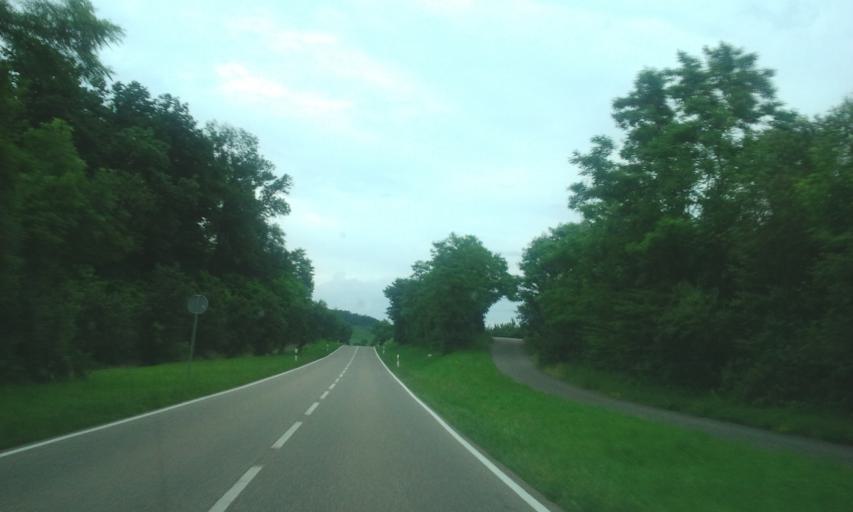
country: DE
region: Baden-Wuerttemberg
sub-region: Karlsruhe Region
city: Illingen
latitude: 48.9630
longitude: 8.9402
